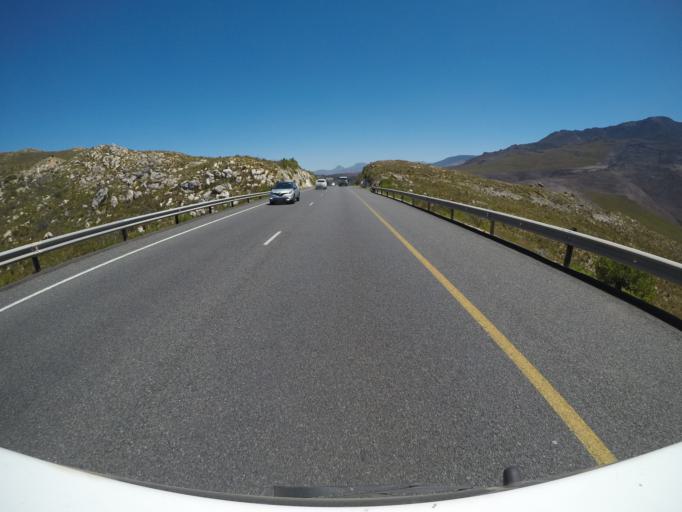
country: ZA
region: Western Cape
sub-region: Overberg District Municipality
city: Grabouw
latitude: -34.2152
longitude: 19.1708
